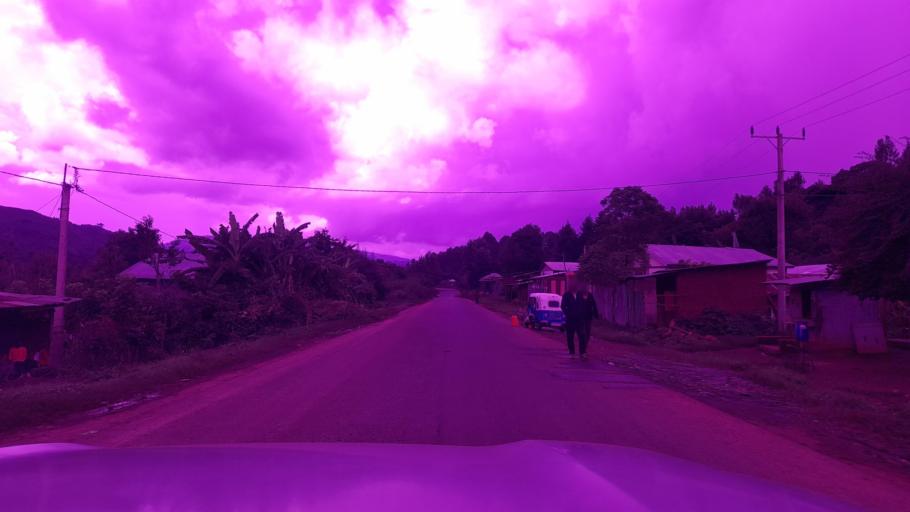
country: ET
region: Oromiya
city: Jima
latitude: 7.6681
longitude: 36.8920
